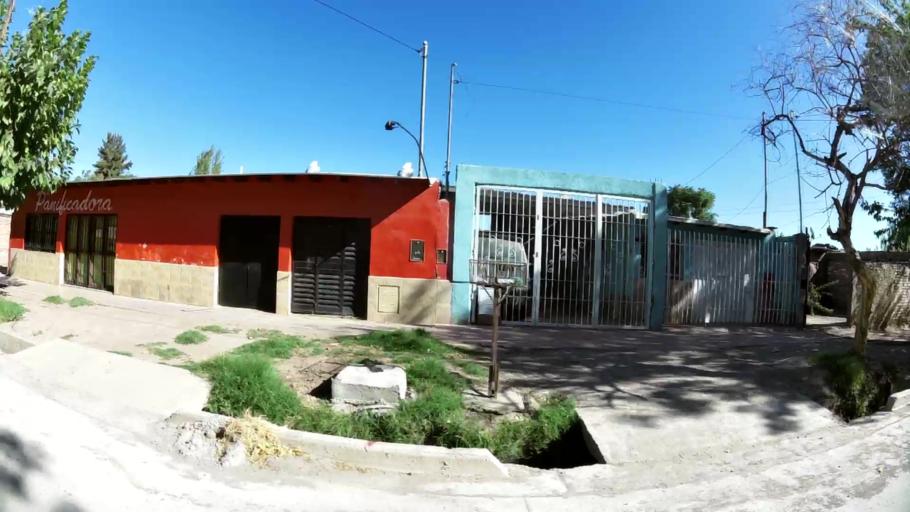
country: AR
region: Mendoza
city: Las Heras
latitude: -32.8325
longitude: -68.8259
